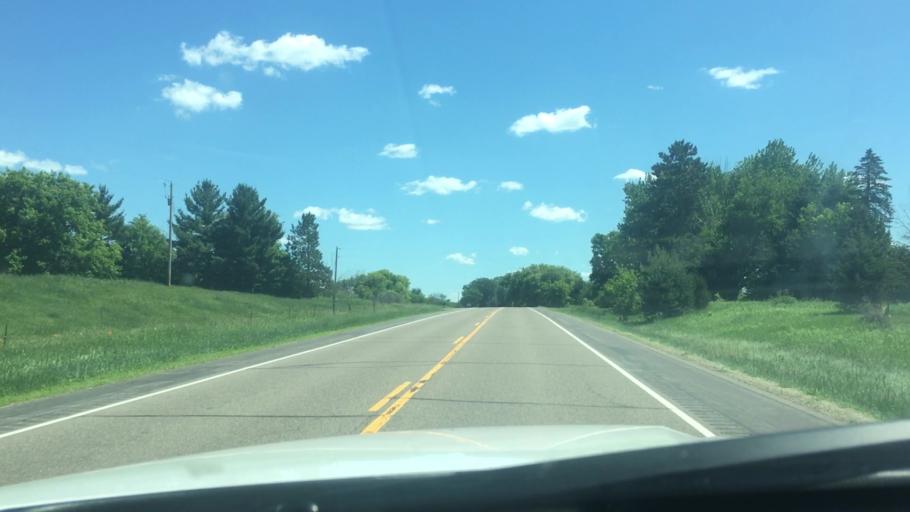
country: US
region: Wisconsin
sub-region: Polk County
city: Osceola
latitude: 45.3463
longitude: -92.7185
